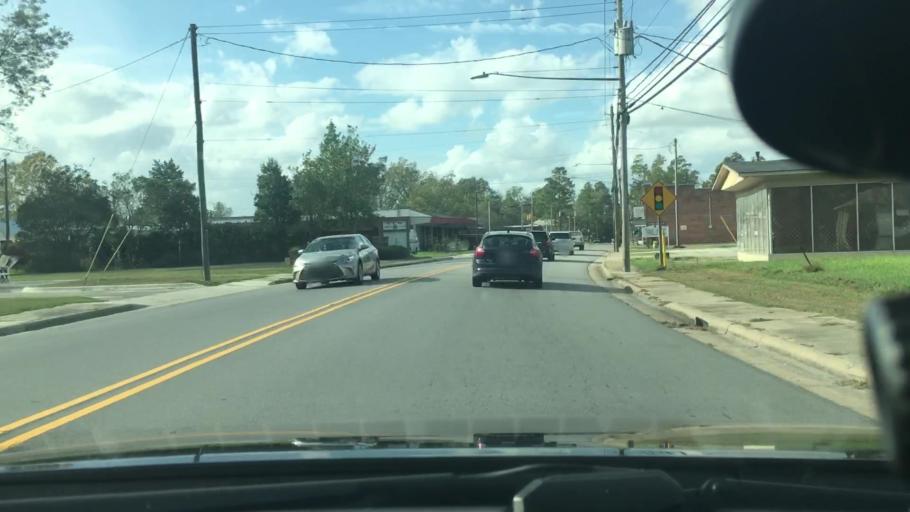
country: US
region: North Carolina
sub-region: Craven County
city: Vanceboro
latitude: 35.2985
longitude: -77.1512
